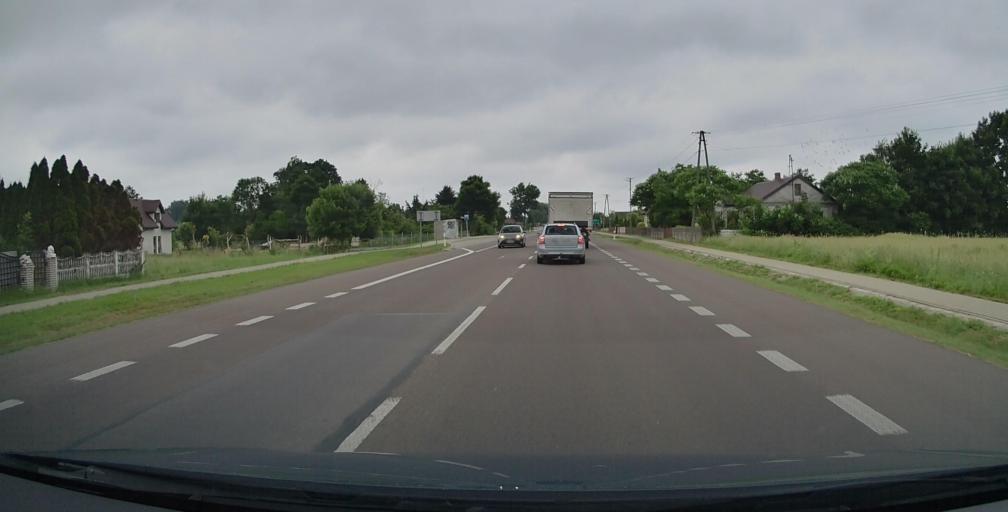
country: PL
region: Lublin Voivodeship
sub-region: Powiat bialski
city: Rzeczyca
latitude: 52.0210
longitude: 22.7225
